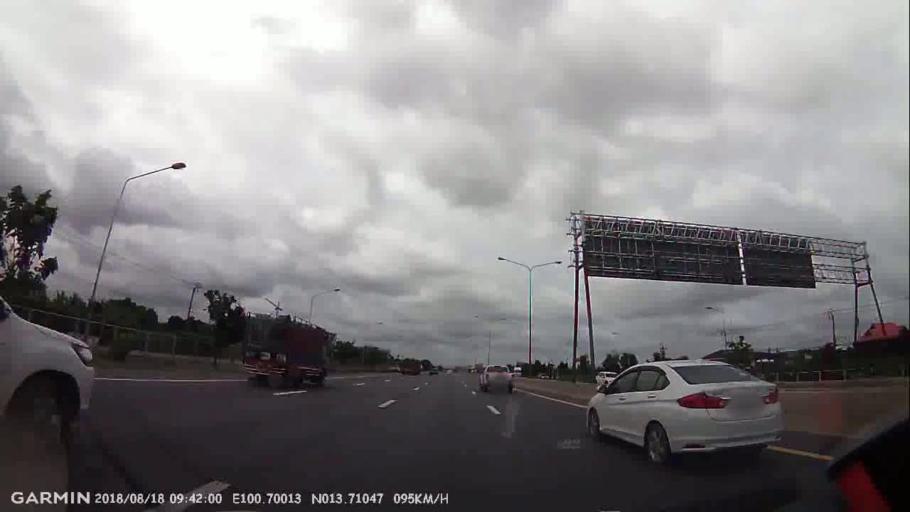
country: TH
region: Bangkok
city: Suan Luang
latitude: 13.7106
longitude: 100.7003
